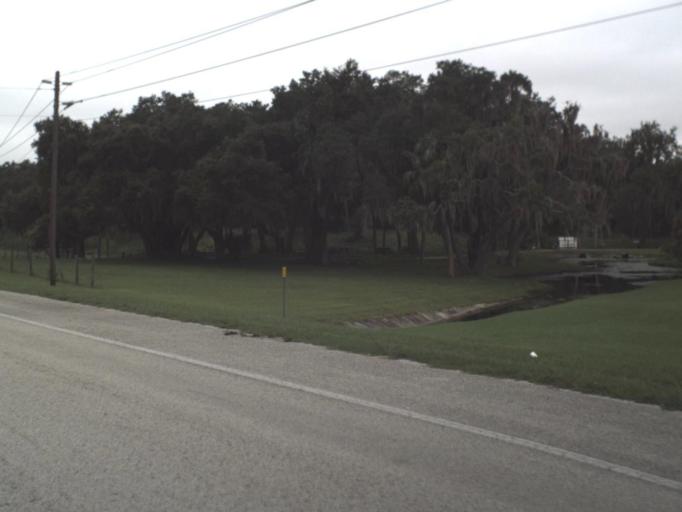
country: US
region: Florida
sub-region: Manatee County
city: Memphis
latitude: 27.5903
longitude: -82.5402
